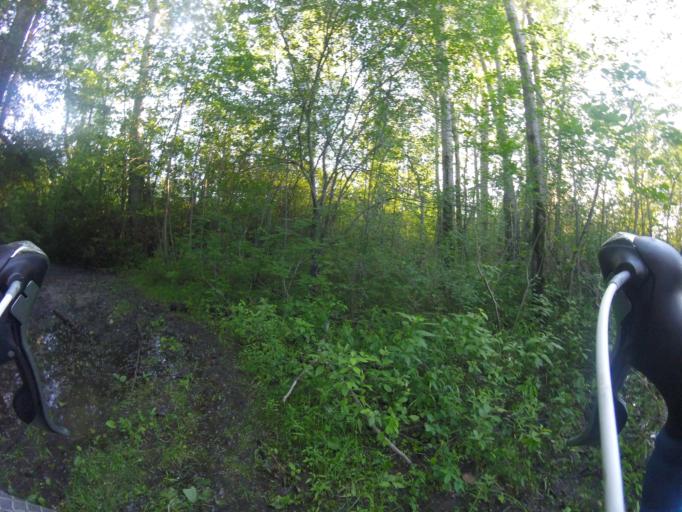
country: CA
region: Ontario
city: Bells Corners
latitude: 45.3612
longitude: -75.8734
